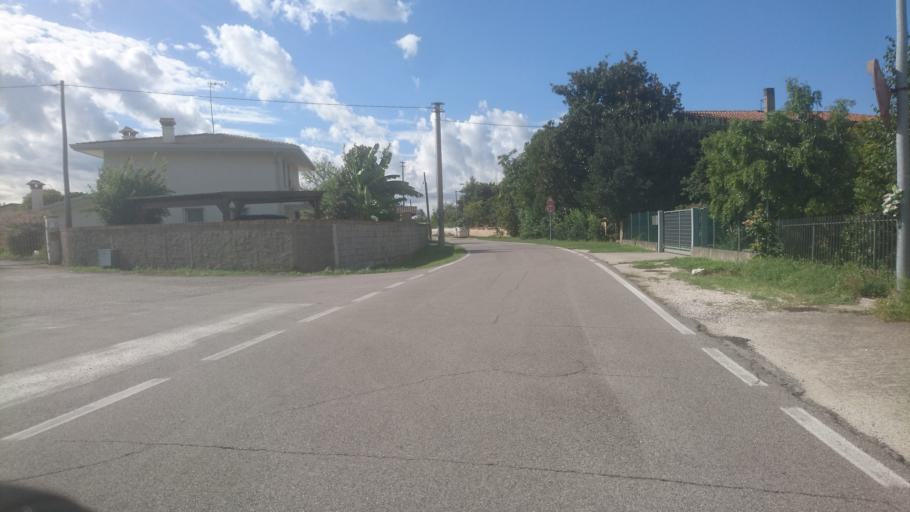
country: IT
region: Veneto
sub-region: Provincia di Venezia
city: Fosso
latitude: 45.3924
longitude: 12.0418
